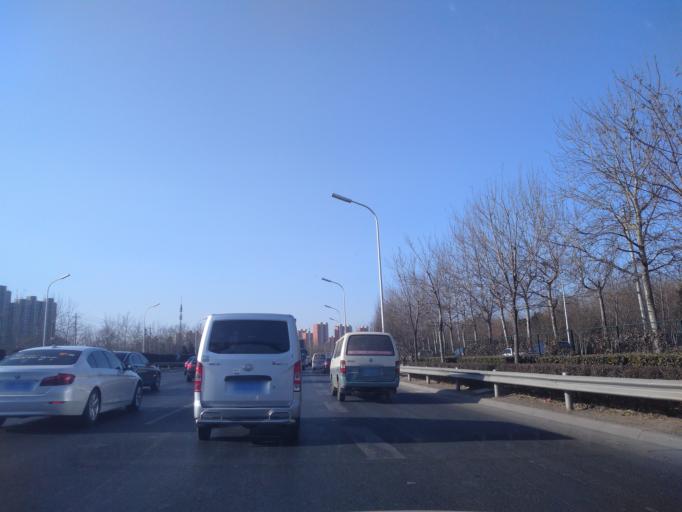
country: CN
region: Beijing
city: Jiugong
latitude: 39.8343
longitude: 116.4617
